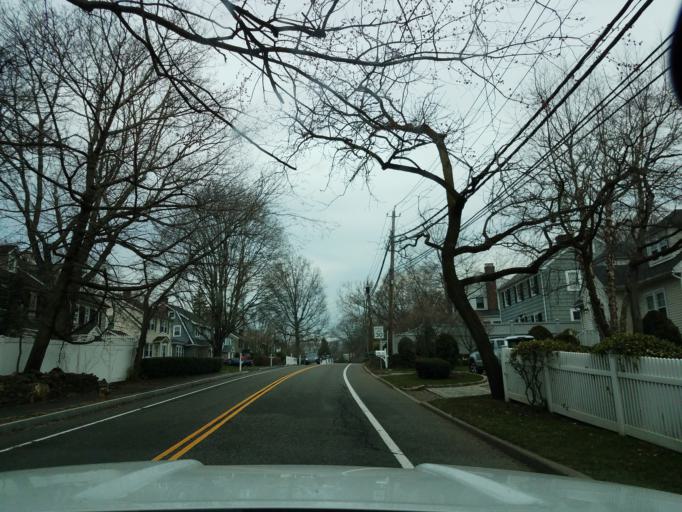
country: US
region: Connecticut
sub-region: Fairfield County
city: Riverside
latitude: 41.0390
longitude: -73.5714
